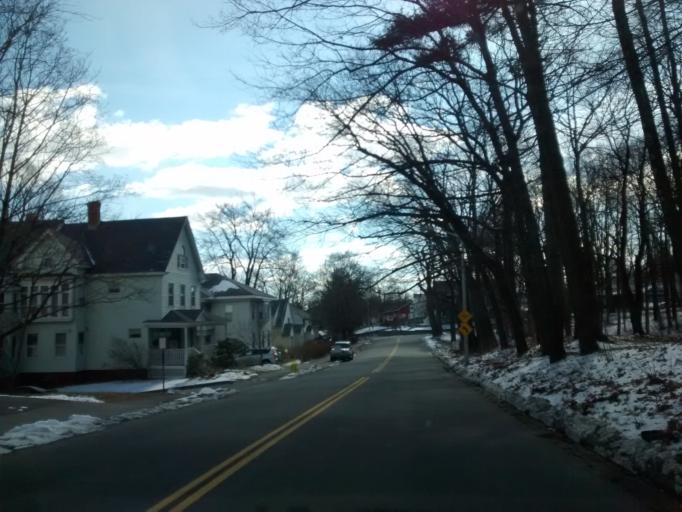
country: US
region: Massachusetts
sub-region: Worcester County
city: Worcester
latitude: 42.2594
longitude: -71.8315
